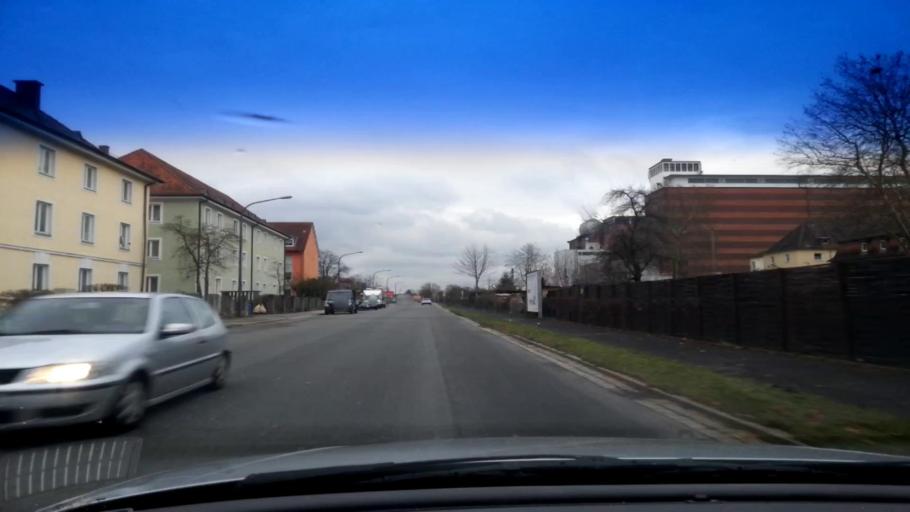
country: DE
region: Bavaria
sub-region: Upper Franconia
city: Bamberg
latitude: 49.8887
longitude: 10.9133
